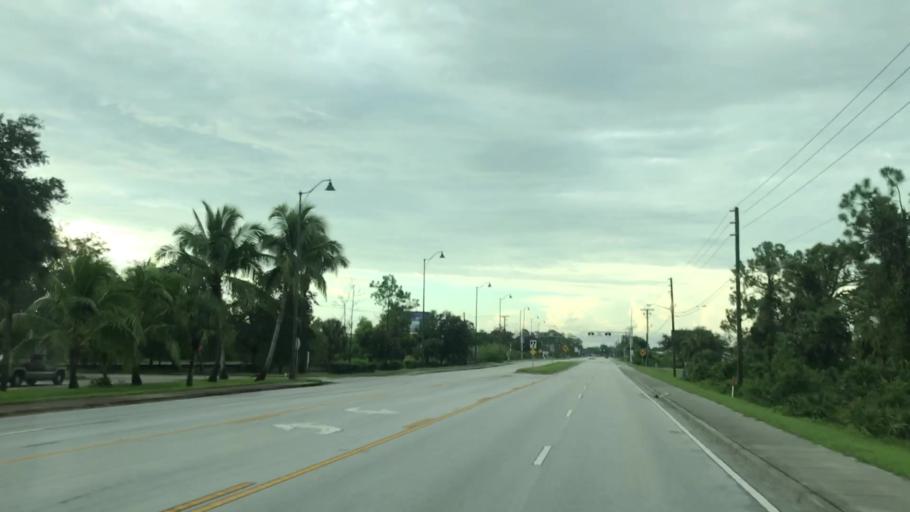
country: US
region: Florida
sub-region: Lee County
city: Bonita Springs
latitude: 26.3780
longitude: -81.8048
